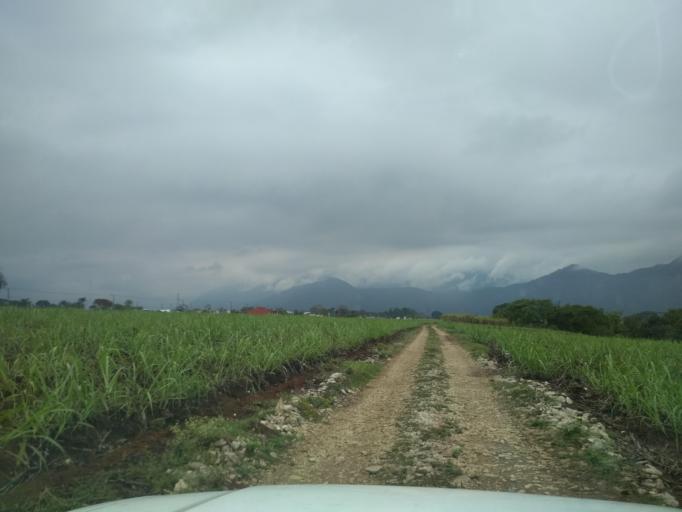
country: MX
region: Veracruz
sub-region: Cordoba
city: San Jose de Tapia
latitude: 18.8489
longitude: -96.9697
